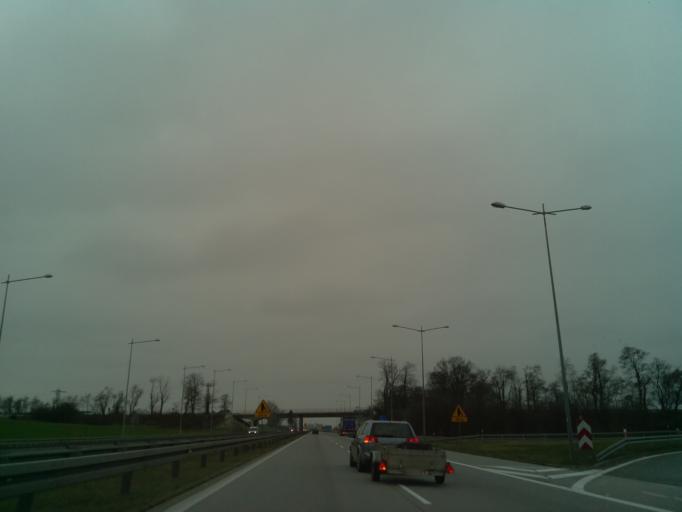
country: PL
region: Lower Silesian Voivodeship
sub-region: Powiat wroclawski
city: Katy Wroclawskie
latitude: 51.0212
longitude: 16.7592
